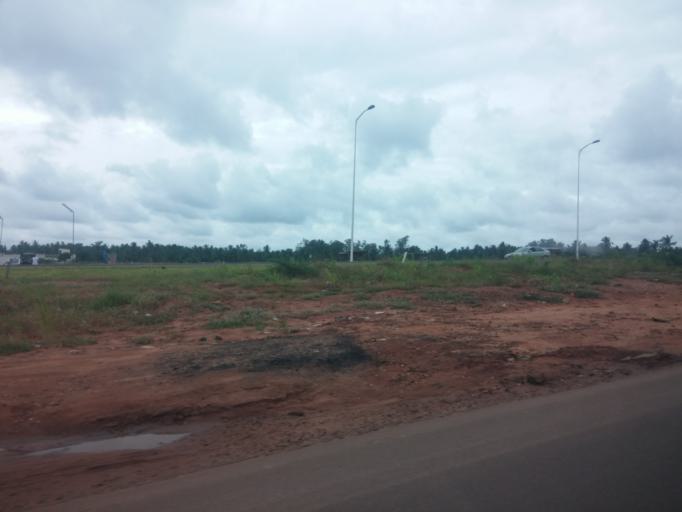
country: TG
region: Maritime
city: Tsevie
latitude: 6.3262
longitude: 1.2189
